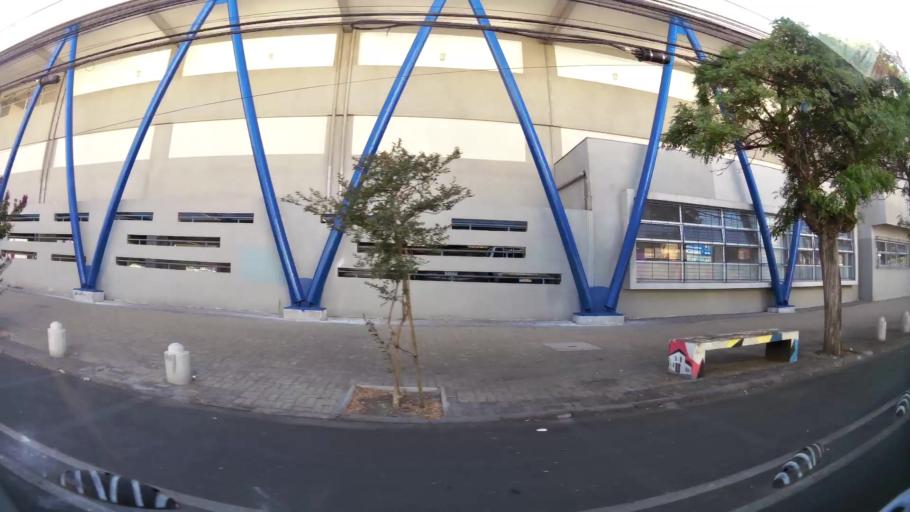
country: CL
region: O'Higgins
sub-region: Provincia de Cachapoal
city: Rancagua
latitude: -34.1713
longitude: -70.7382
